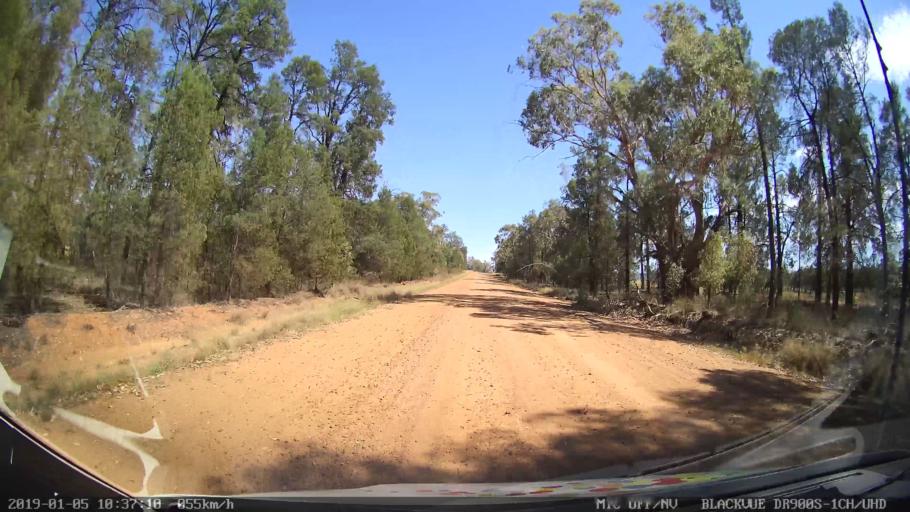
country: AU
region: New South Wales
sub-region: Gilgandra
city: Gilgandra
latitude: -31.4767
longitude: 148.9225
